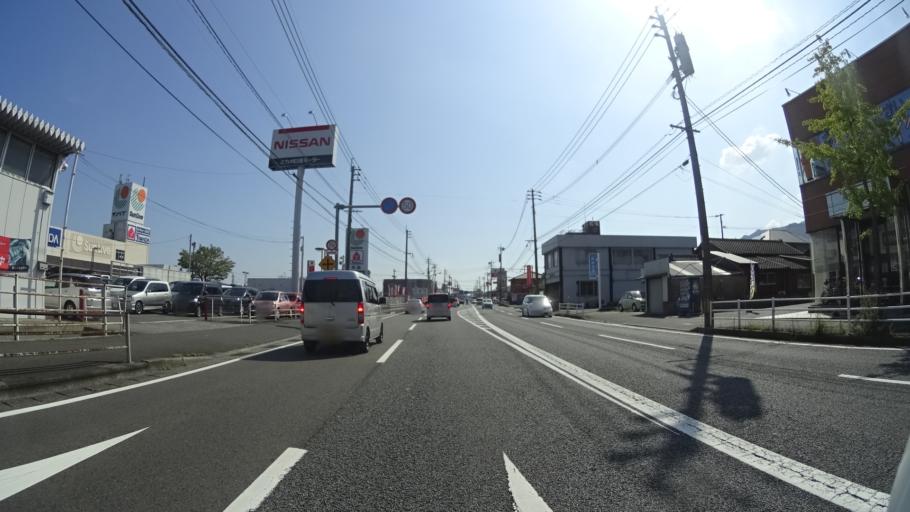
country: JP
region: Fukuoka
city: Kanda
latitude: 33.7747
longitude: 130.9825
